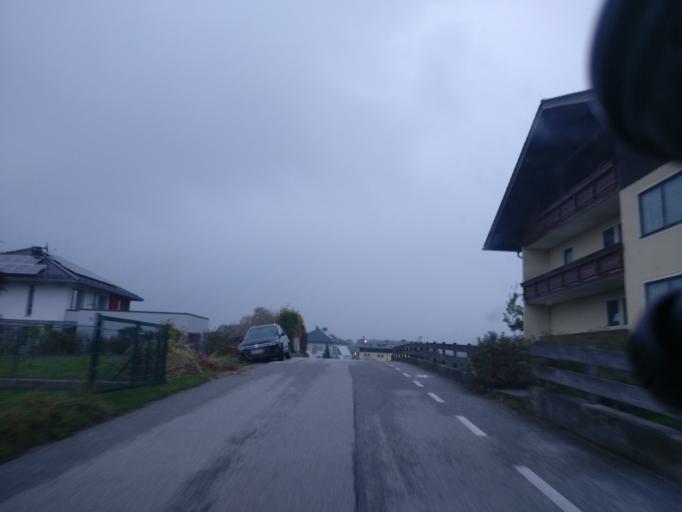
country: AT
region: Salzburg
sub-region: Politischer Bezirk Salzburg-Umgebung
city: Elixhausen
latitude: 47.8673
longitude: 13.0708
